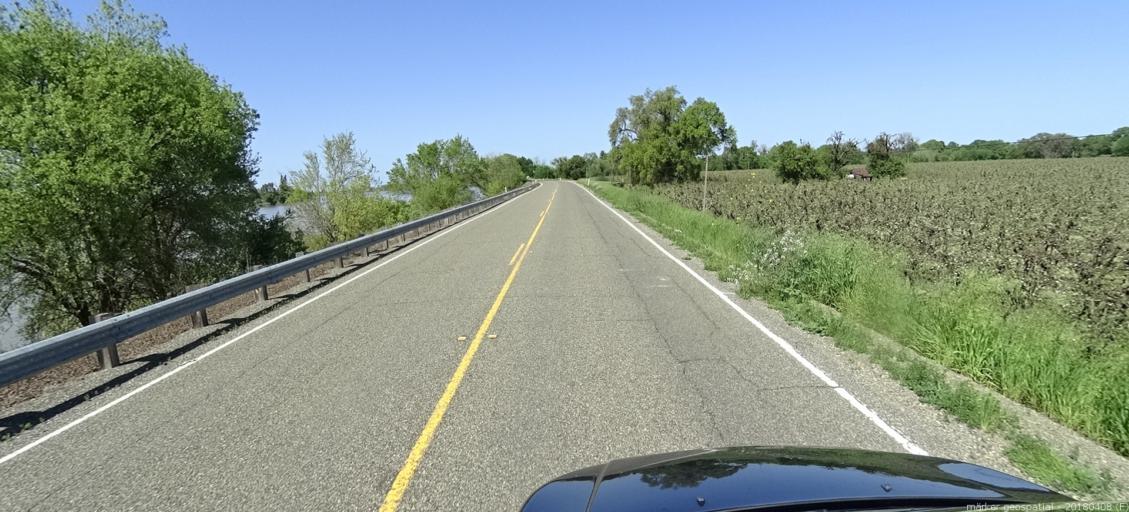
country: US
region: California
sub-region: Sacramento County
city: Laguna
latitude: 38.3954
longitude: -121.5119
